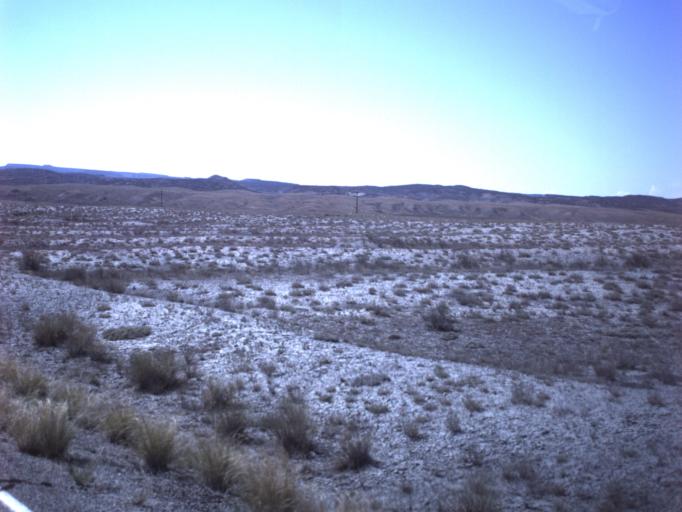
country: US
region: Utah
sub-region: Grand County
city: Moab
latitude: 38.8913
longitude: -109.3111
